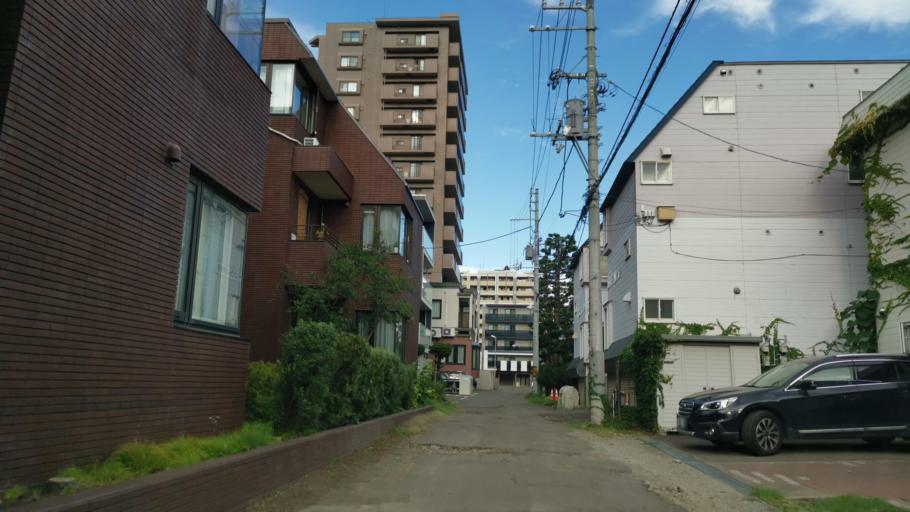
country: JP
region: Hokkaido
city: Sapporo
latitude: 43.0450
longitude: 141.3346
